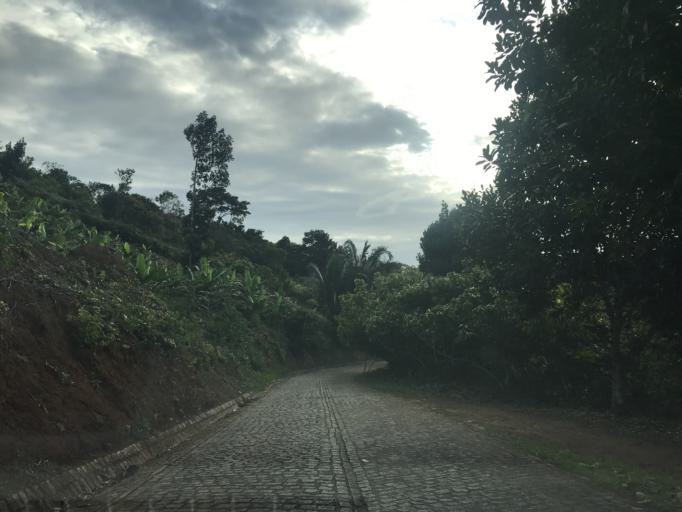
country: BR
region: Bahia
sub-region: Gandu
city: Gandu
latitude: -13.8997
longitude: -39.4726
